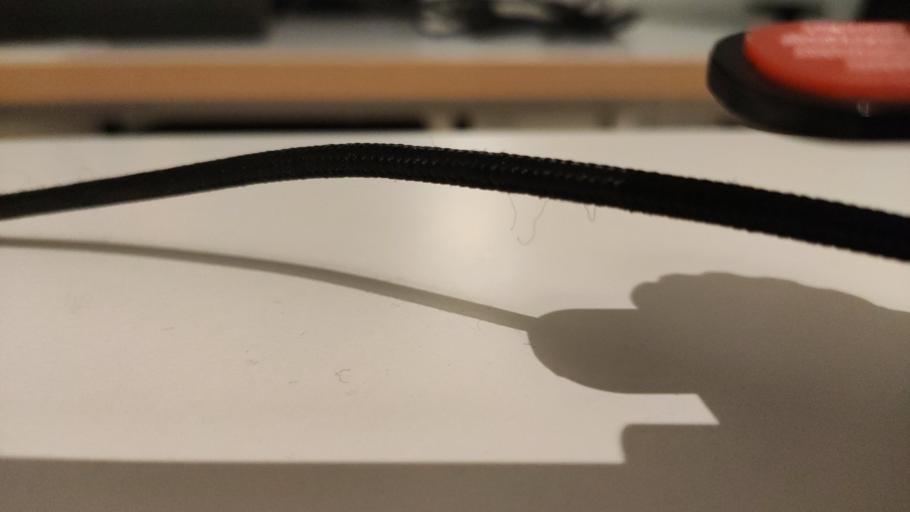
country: RU
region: Moskovskaya
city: Rogachevo
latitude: 56.4088
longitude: 37.2354
